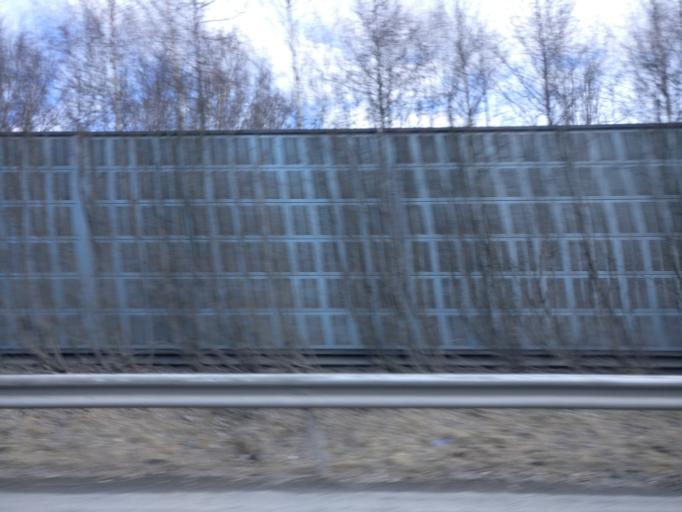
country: FI
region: Haeme
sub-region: Haemeenlinna
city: Haemeenlinna
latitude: 60.9816
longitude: 24.4681
